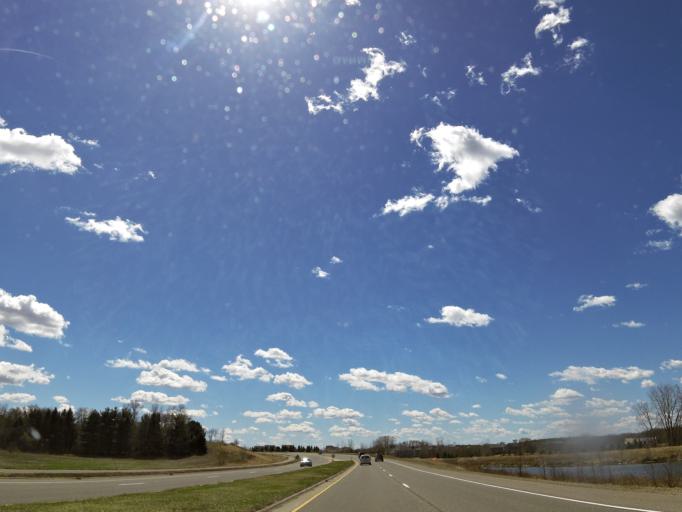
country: US
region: Minnesota
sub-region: Washington County
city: Cottage Grove
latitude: 44.8655
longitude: -92.9474
